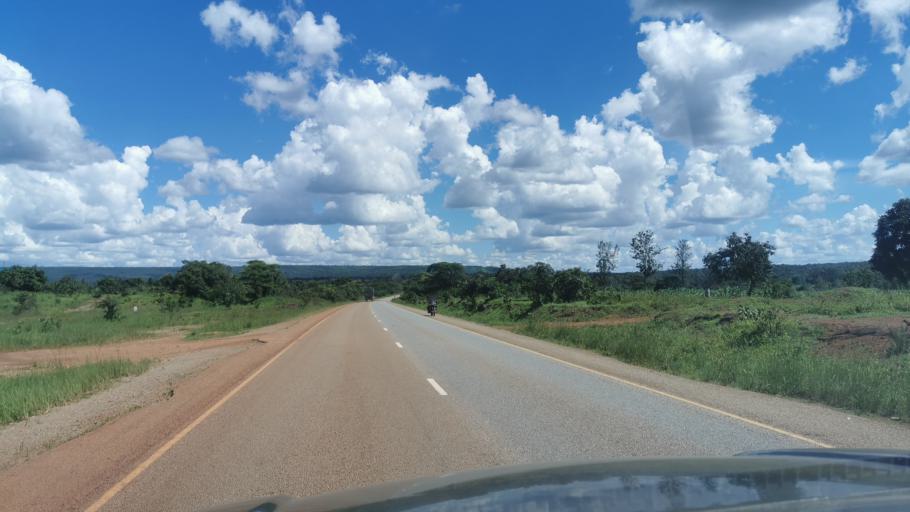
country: TZ
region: Kigoma
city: Kakonko
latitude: -3.0440
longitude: 31.2452
